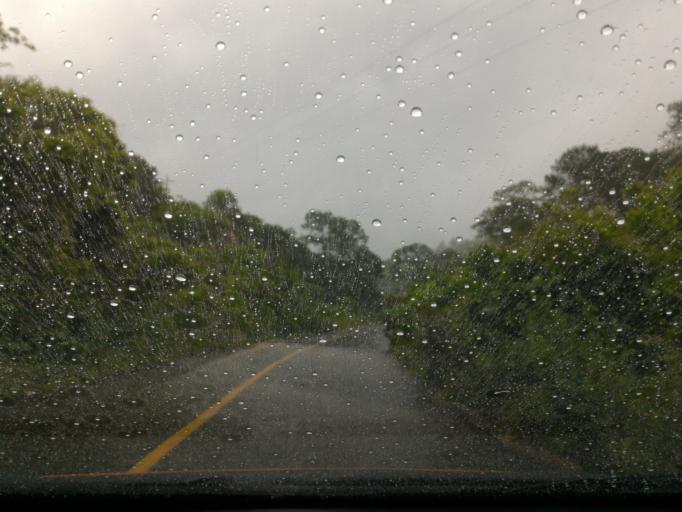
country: MX
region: Jalisco
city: San Andres Ixtlan
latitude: 19.8343
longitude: -103.4594
